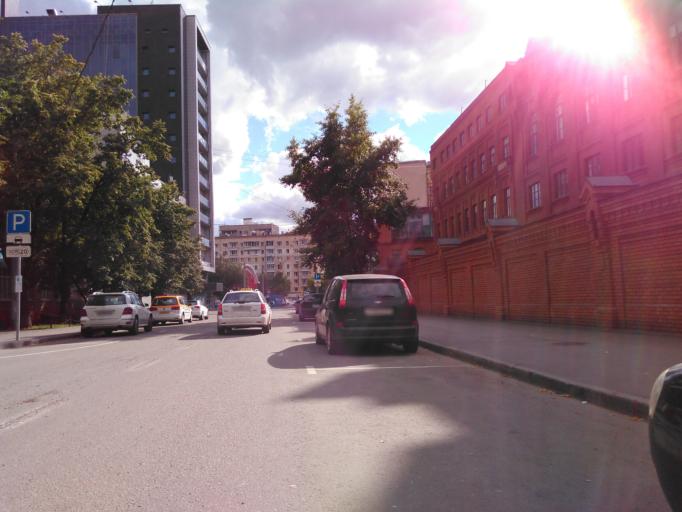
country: RU
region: Moskovskaya
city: Dorogomilovo
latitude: 55.7313
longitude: 37.5735
